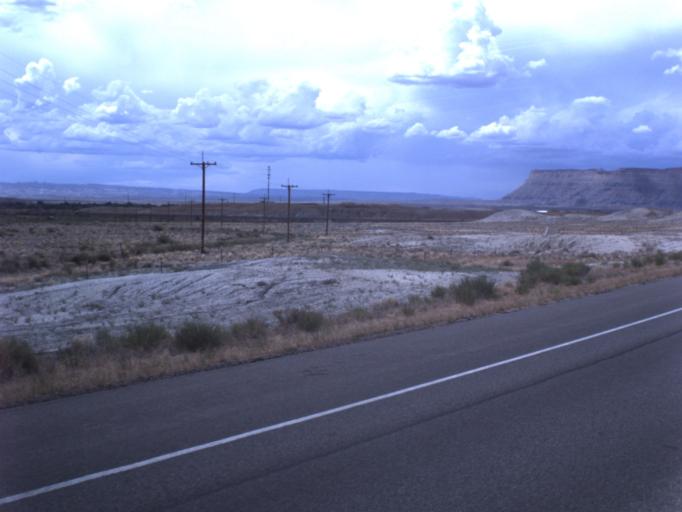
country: US
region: Utah
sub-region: Carbon County
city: East Carbon City
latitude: 38.9797
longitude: -110.1218
